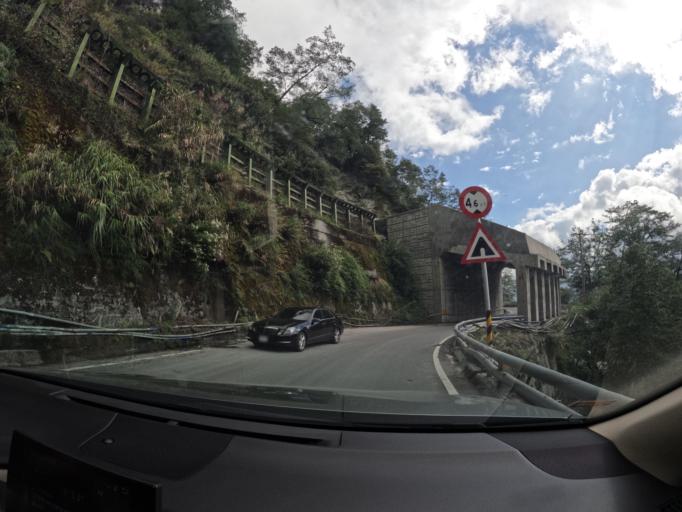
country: TW
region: Taiwan
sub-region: Taitung
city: Taitung
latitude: 23.2334
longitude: 121.0075
